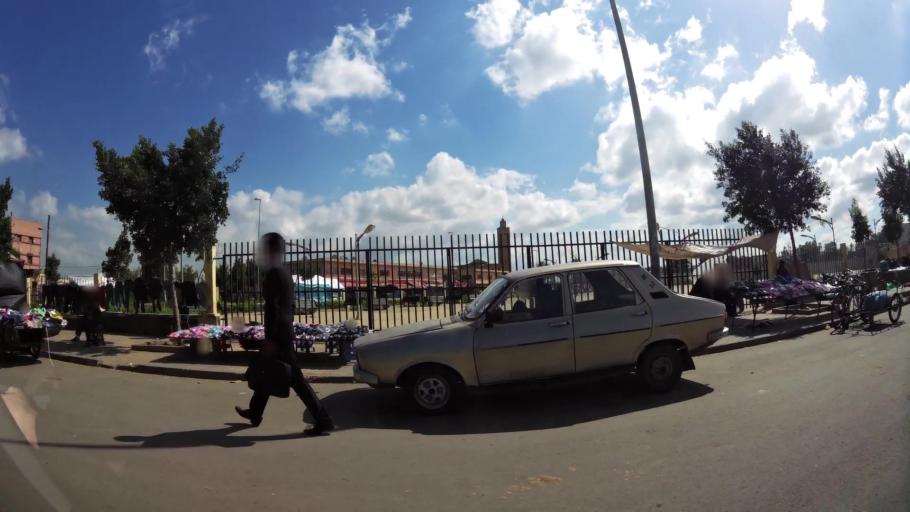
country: MA
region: Grand Casablanca
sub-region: Mediouna
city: Mediouna
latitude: 33.4537
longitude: -7.5169
